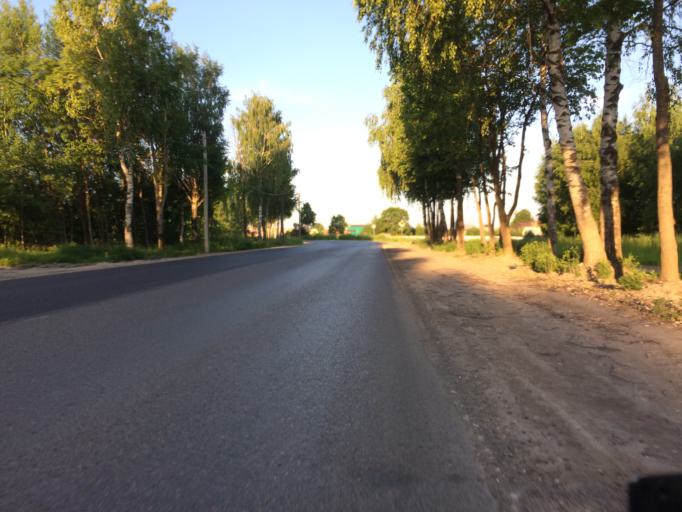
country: RU
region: Mariy-El
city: Medvedevo
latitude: 56.6504
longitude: 47.8324
